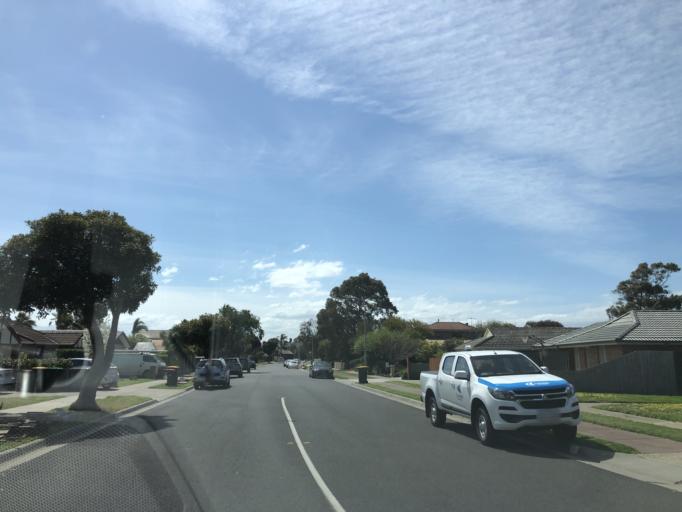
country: AU
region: Victoria
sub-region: Kingston
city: Patterson Lakes
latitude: -38.0747
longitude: 145.1442
